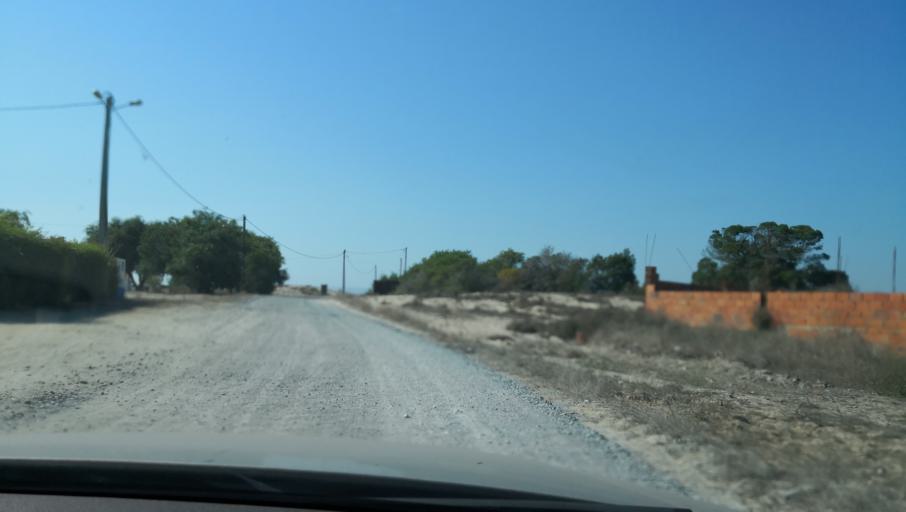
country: PT
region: Setubal
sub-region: Setubal
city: Setubal
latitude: 38.3966
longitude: -8.7833
